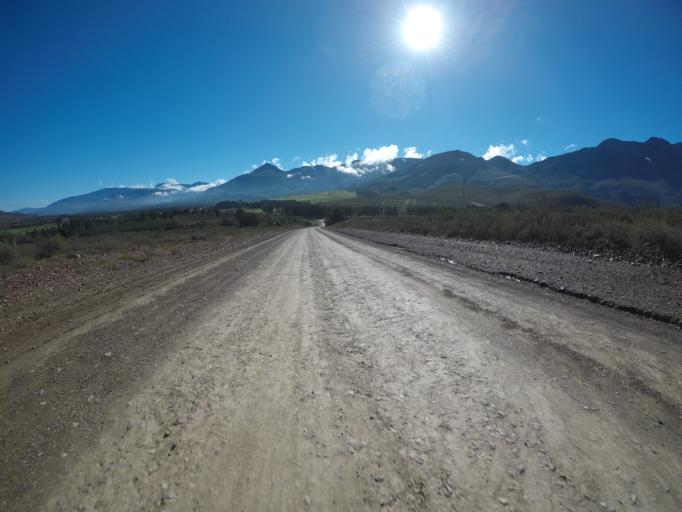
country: ZA
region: Western Cape
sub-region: Overberg District Municipality
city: Caledon
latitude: -34.0797
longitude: 19.6452
